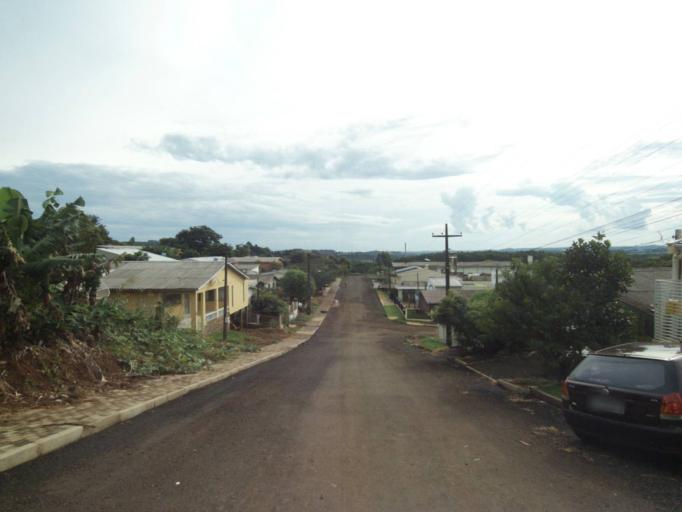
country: BR
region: Parana
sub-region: Guaraniacu
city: Guaraniacu
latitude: -25.1026
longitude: -52.8765
